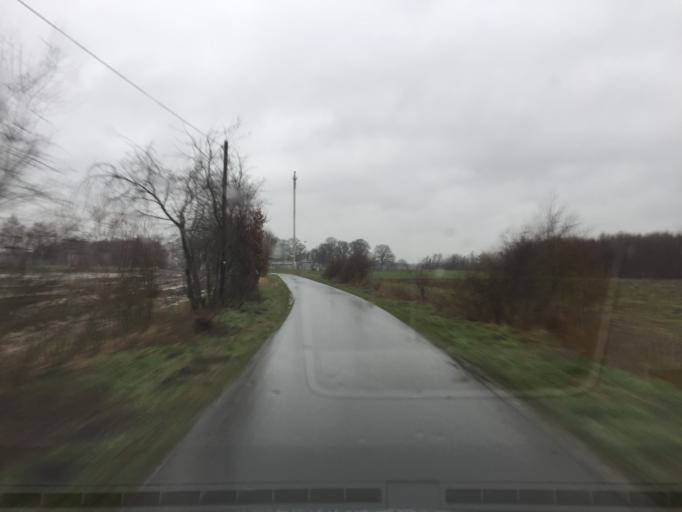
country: DE
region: Lower Saxony
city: Borstel
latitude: 52.6300
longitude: 8.9257
